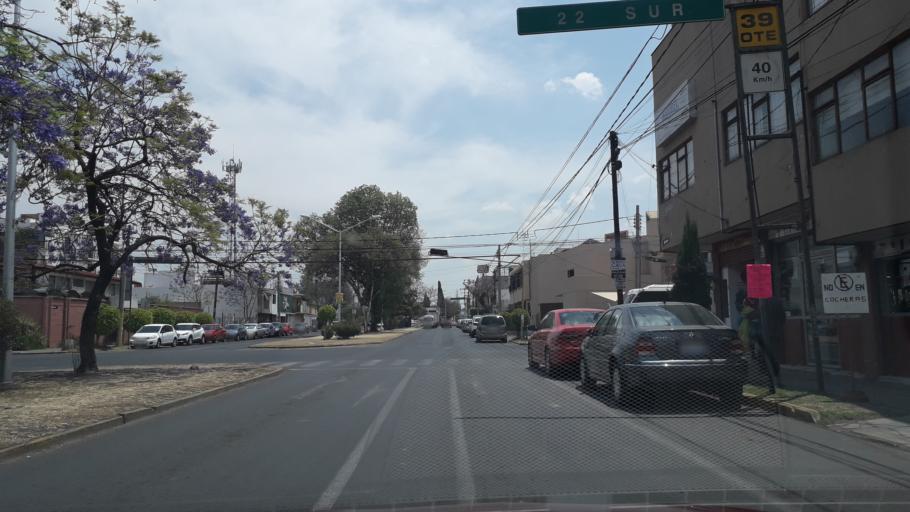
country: MX
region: Puebla
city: Puebla
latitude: 19.0217
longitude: -98.1934
